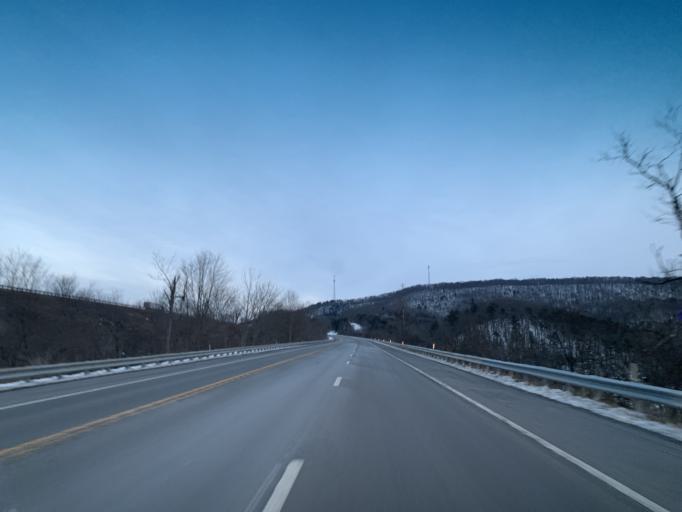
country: US
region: Maryland
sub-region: Allegany County
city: Cumberland
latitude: 39.6948
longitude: -78.5462
